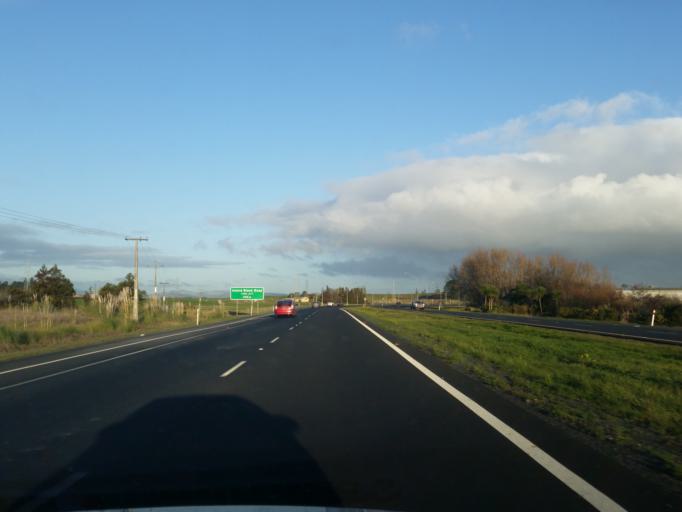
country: NZ
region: Waikato
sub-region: Waikato District
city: Te Kauwhata
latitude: -37.3038
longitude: 175.0636
